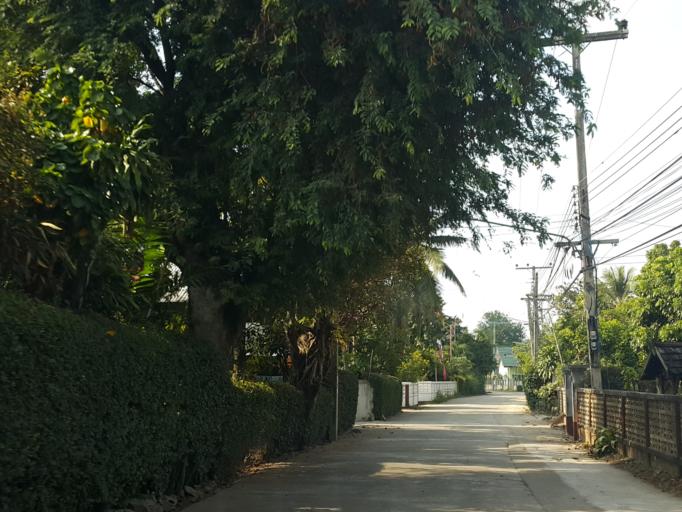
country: TH
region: Chiang Mai
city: San Sai
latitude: 18.8265
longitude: 99.1236
